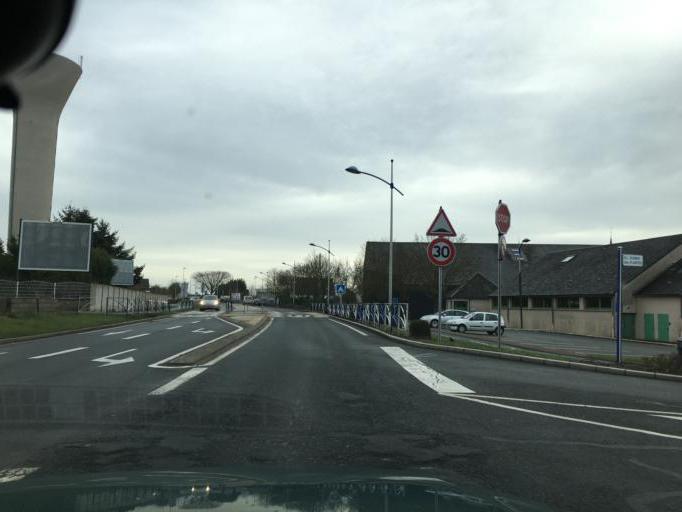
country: FR
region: Centre
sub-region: Departement du Loiret
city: Ormes
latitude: 47.9425
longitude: 1.8138
